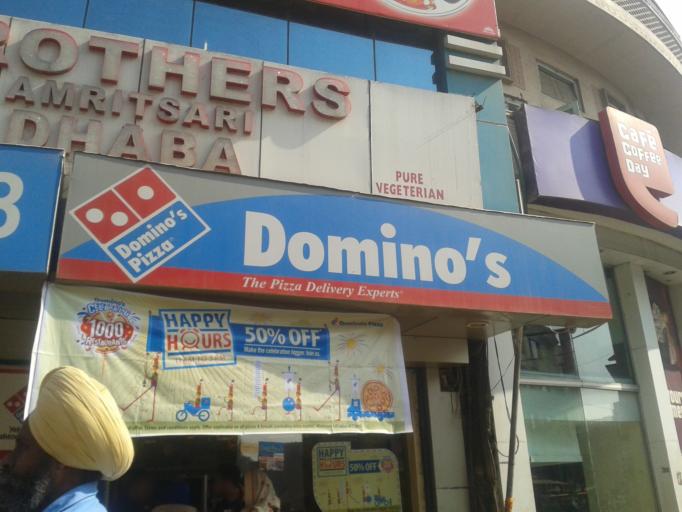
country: IN
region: Punjab
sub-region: Amritsar
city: Amritsar
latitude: 31.6226
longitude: 74.8796
